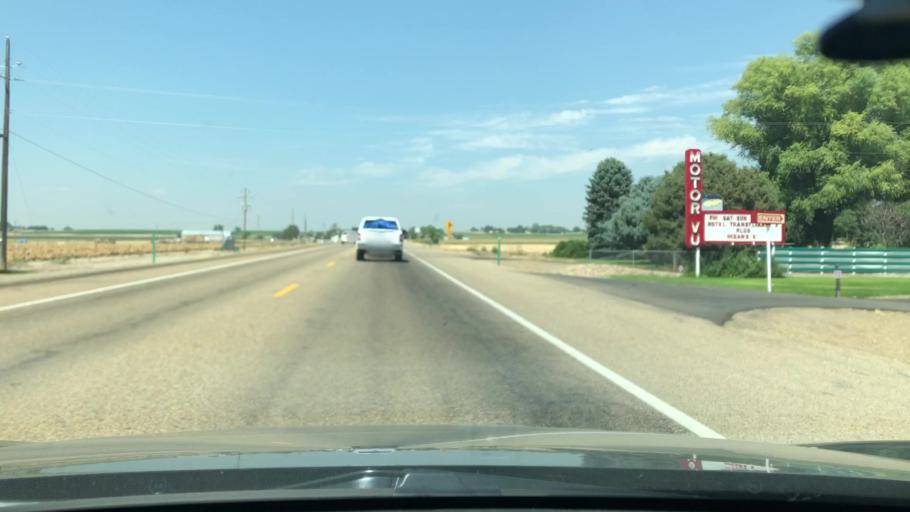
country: US
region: Idaho
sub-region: Canyon County
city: Parma
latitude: 43.8001
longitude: -116.9522
